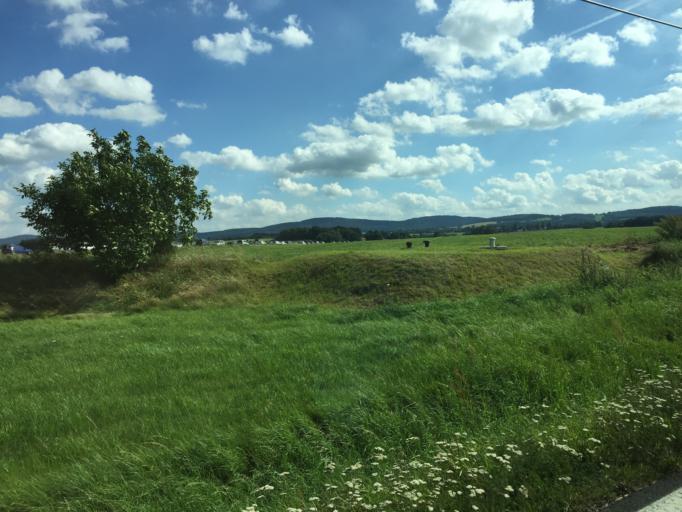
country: DE
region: Saxony
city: Kubschutz
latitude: 51.1858
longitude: 14.5126
